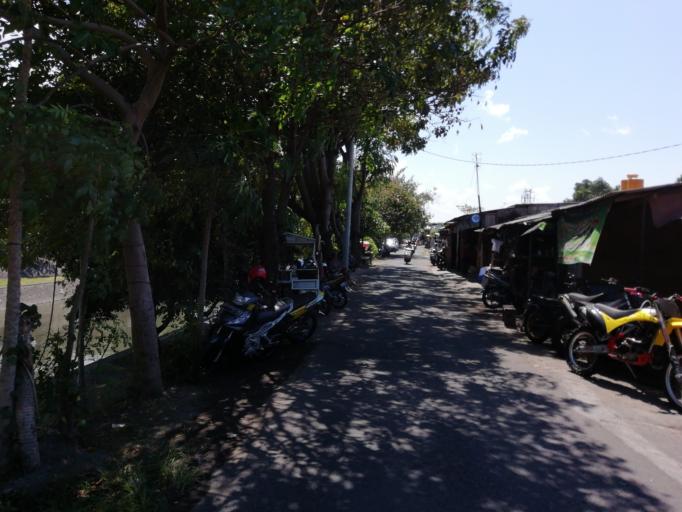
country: ID
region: Bali
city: Karyadharma
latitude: -8.6914
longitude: 115.1975
